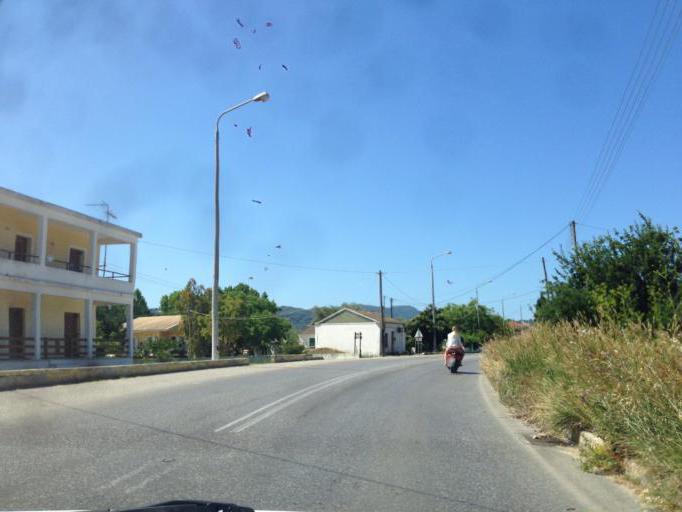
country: GR
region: Ionian Islands
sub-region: Nomos Kerkyras
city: Agios Georgis
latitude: 39.7550
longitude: 19.7185
